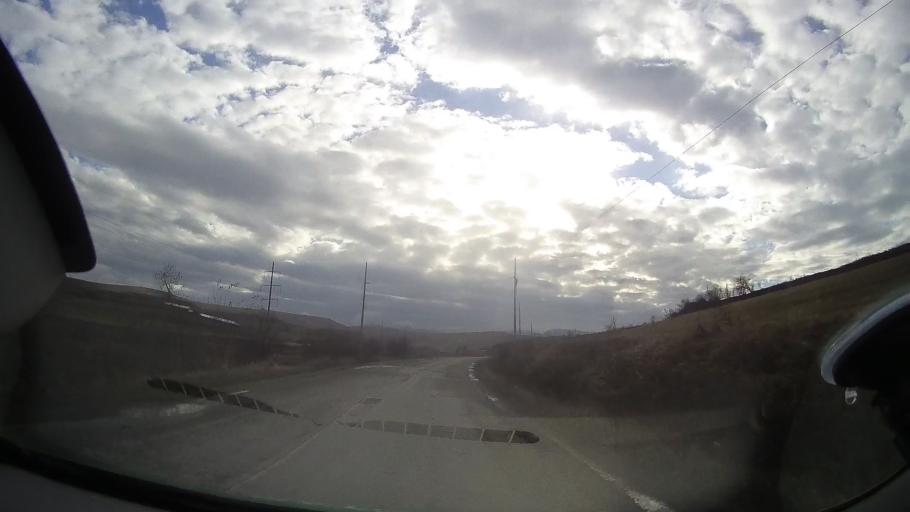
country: RO
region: Cluj
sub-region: Comuna Baisoara
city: Baisoara
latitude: 46.6069
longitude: 23.4586
